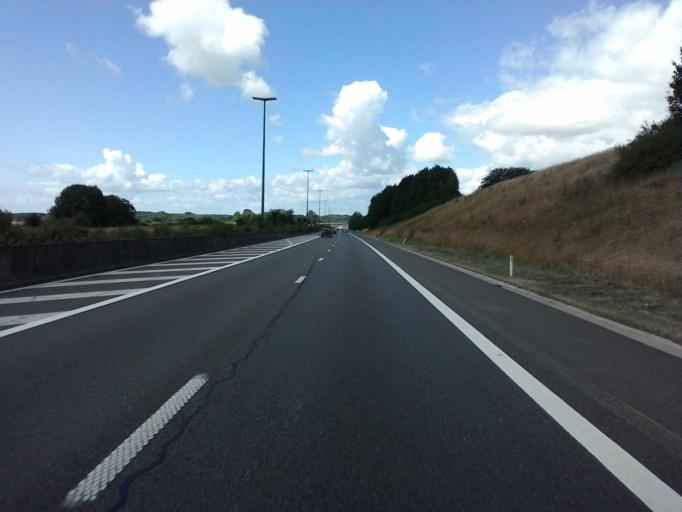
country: BE
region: Wallonia
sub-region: Province du Luxembourg
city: Habay-la-Vieille
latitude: 49.6960
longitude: 5.6924
